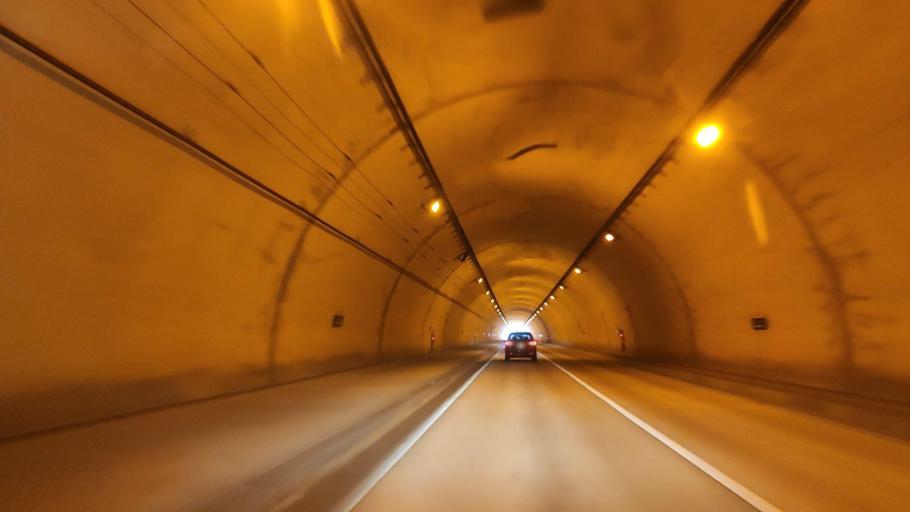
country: JP
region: Ehime
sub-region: Shikoku-chuo Shi
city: Matsuyama
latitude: 33.8849
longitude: 132.7085
